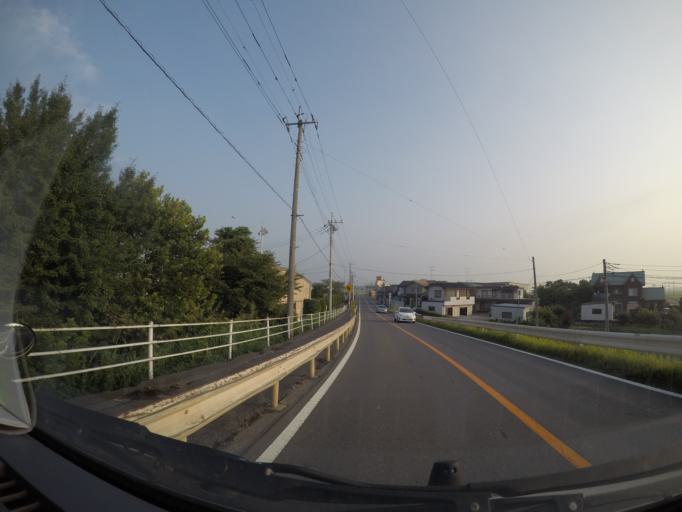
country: JP
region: Tochigi
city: Fujioka
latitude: 36.2731
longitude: 139.7134
